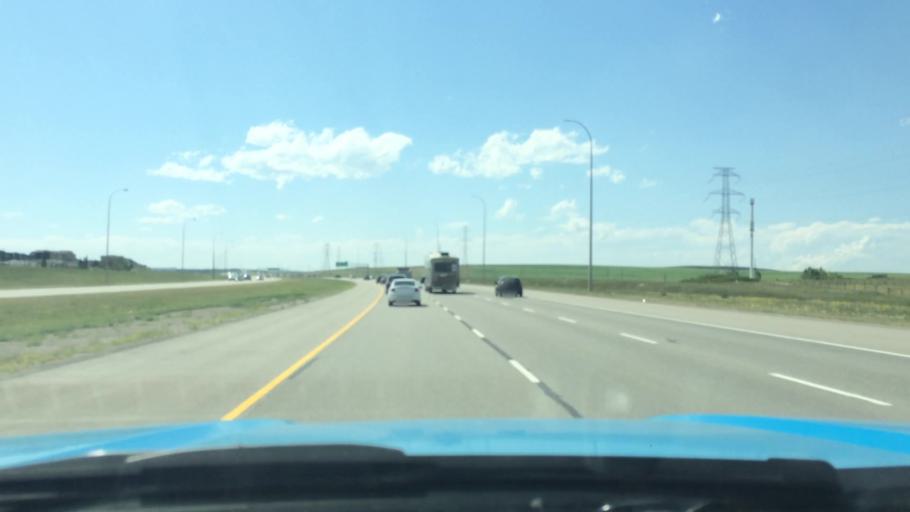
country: CA
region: Alberta
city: Airdrie
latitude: 51.1759
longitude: -114.0410
